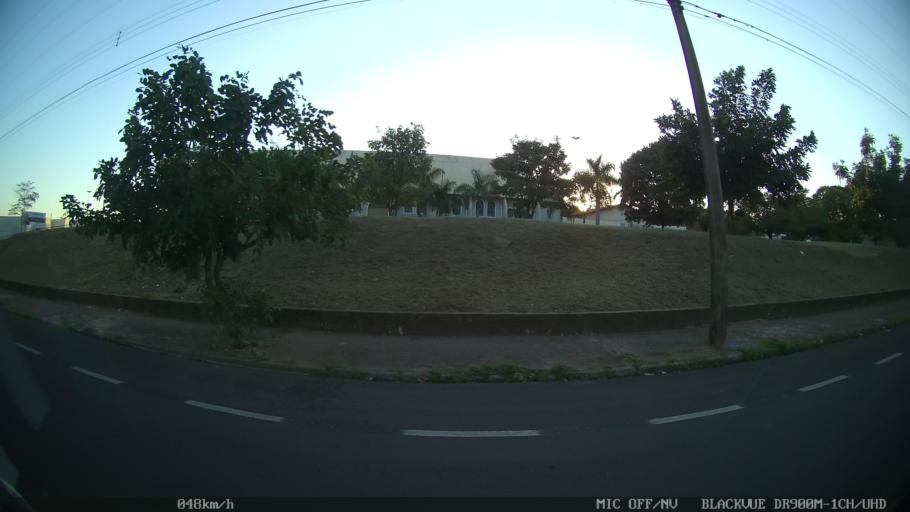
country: BR
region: Sao Paulo
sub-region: Sao Jose Do Rio Preto
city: Sao Jose do Rio Preto
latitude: -20.8043
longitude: -49.3606
